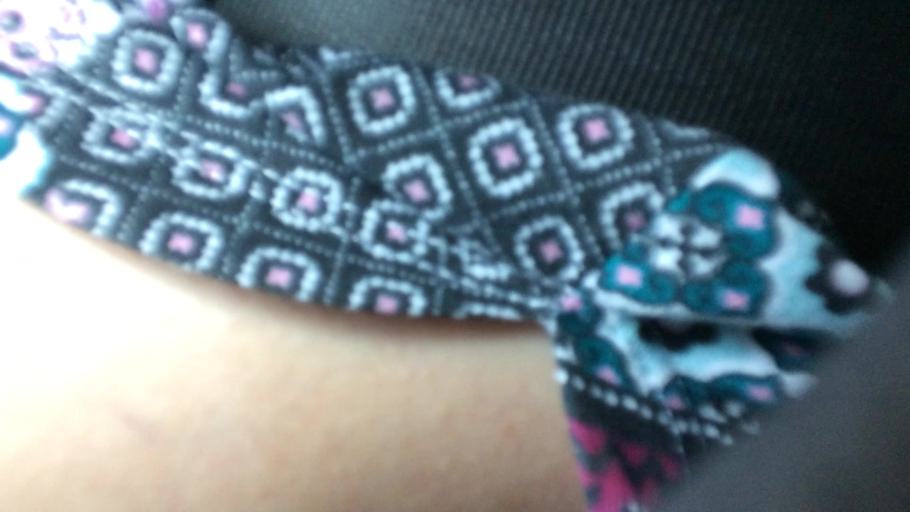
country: US
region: New Mexico
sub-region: Colfax County
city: Springer
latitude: 36.2384
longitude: -104.6519
